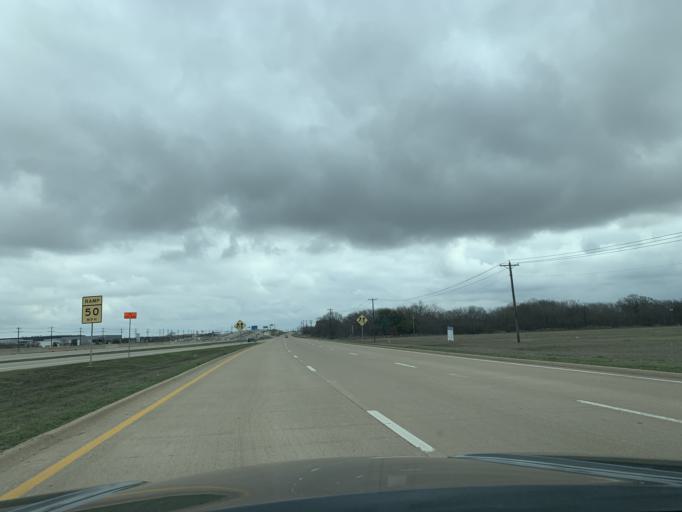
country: US
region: Texas
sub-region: Collin County
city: Allen
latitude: 33.1354
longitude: -96.7021
